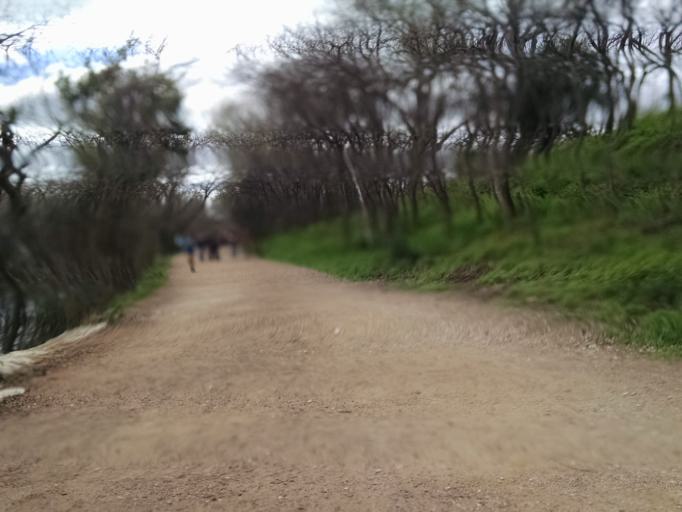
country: US
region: Texas
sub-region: Travis County
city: Austin
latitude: 30.2662
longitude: -97.7636
